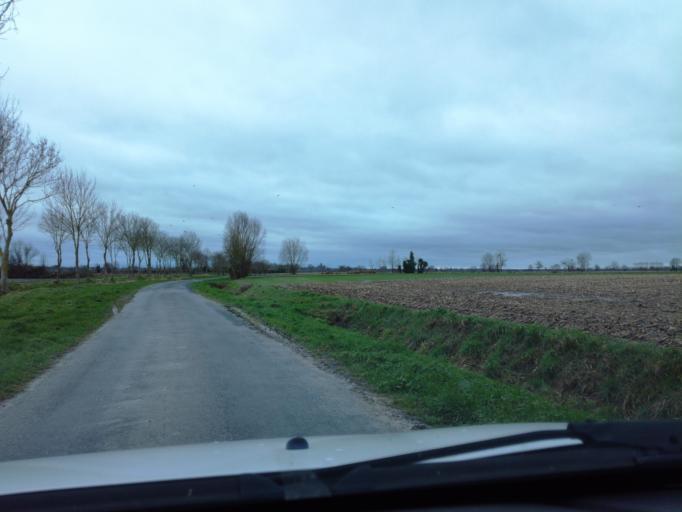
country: FR
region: Brittany
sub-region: Departement d'Ille-et-Vilaine
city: Baguer-Pican
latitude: 48.5706
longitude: -1.7232
